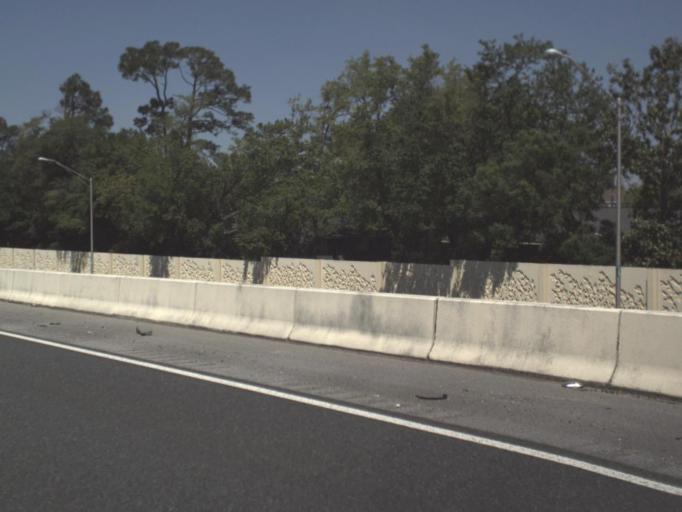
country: US
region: Florida
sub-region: Escambia County
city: Ferry Pass
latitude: 30.5038
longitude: -87.2227
